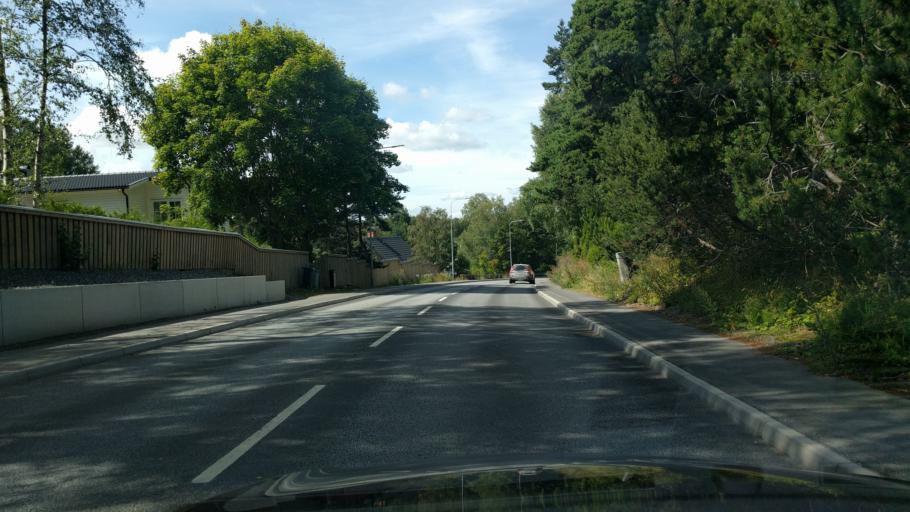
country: SE
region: Stockholm
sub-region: Taby Kommun
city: Taby
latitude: 59.4504
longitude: 18.0587
